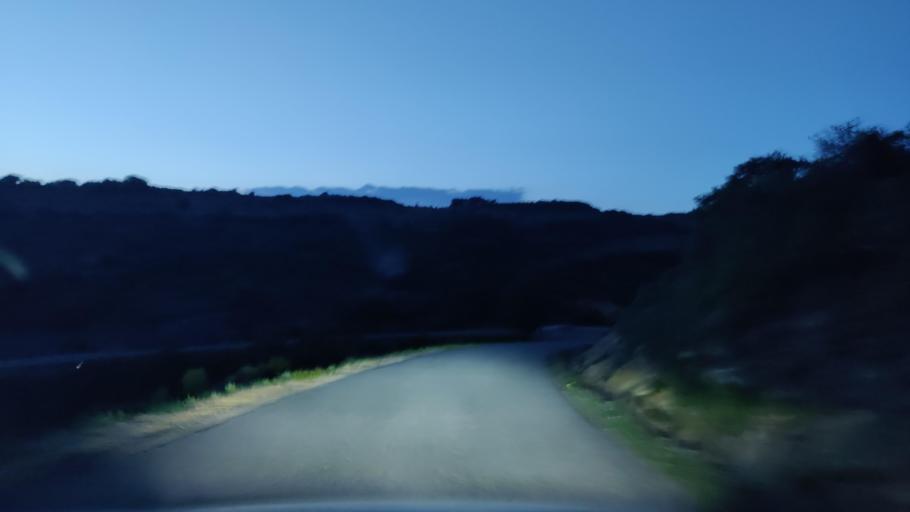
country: FR
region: Languedoc-Roussillon
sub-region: Departement des Pyrenees-Orientales
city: Estagel
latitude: 42.8824
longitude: 2.7478
